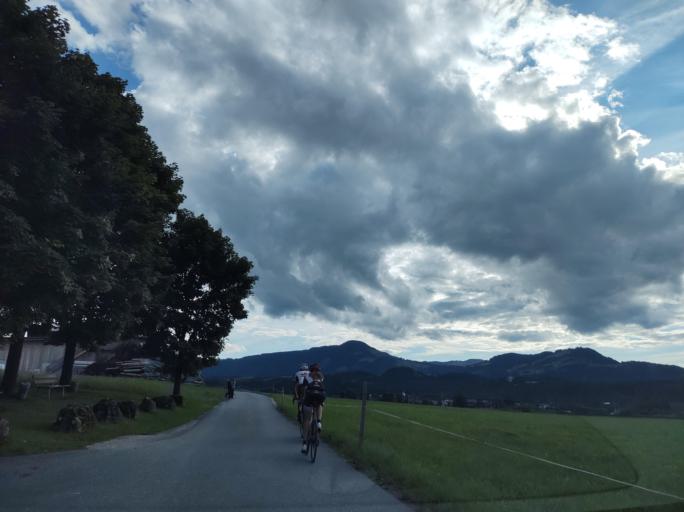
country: AT
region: Tyrol
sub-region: Politischer Bezirk Kitzbuhel
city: Oberndorf in Tirol
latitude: 47.5032
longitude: 12.3999
